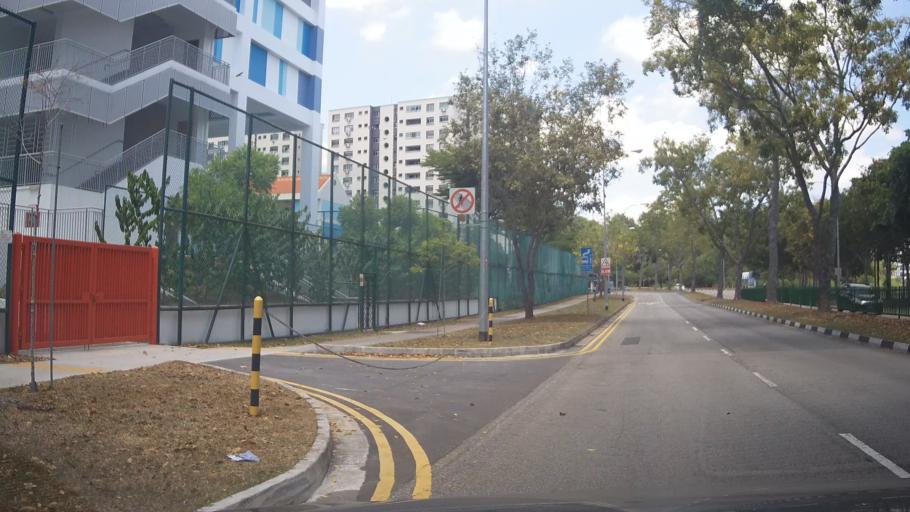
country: MY
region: Johor
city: Kampung Pasir Gudang Baru
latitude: 1.3716
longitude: 103.9638
